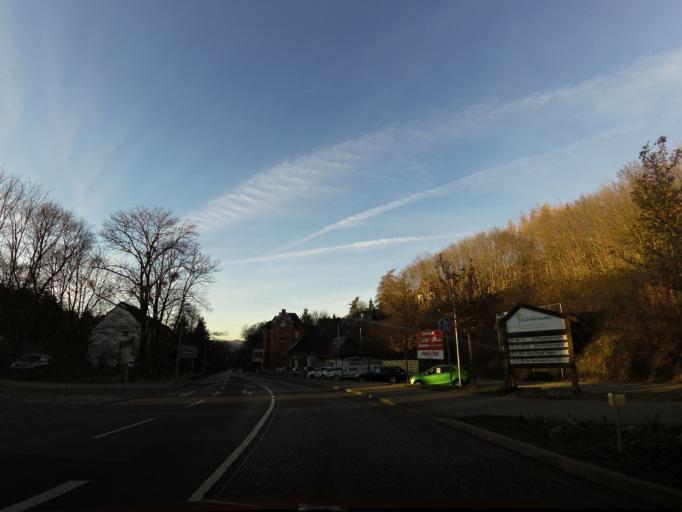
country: DE
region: Saxony-Anhalt
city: Blankenburg
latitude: 51.7843
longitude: 10.9672
